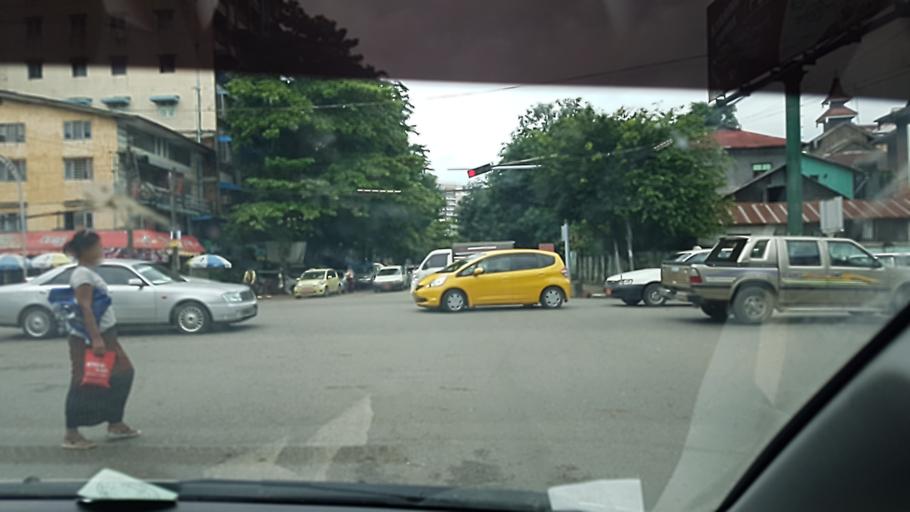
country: MM
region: Yangon
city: Yangon
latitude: 16.8040
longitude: 96.1298
